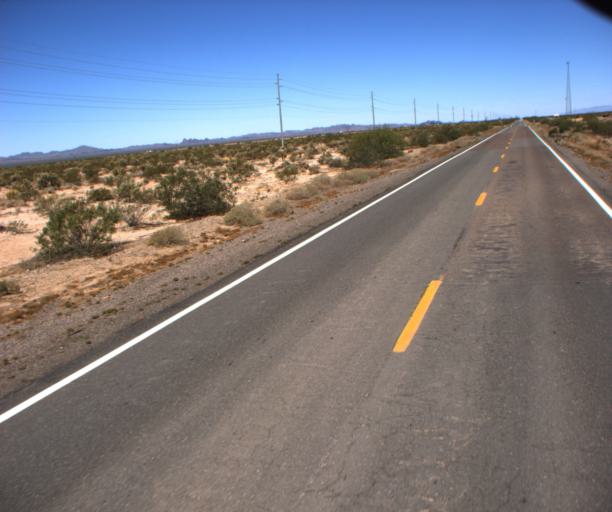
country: US
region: Arizona
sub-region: La Paz County
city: Salome
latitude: 33.8325
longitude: -113.8786
